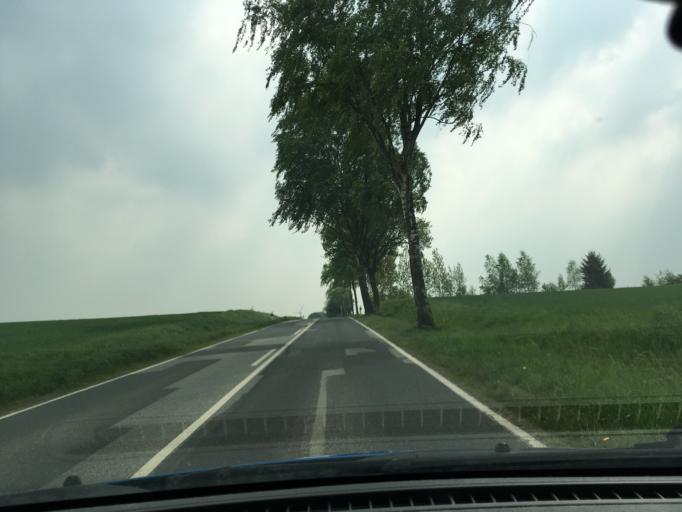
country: DE
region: Lower Saxony
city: Seevetal
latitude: 53.4155
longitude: 9.8954
